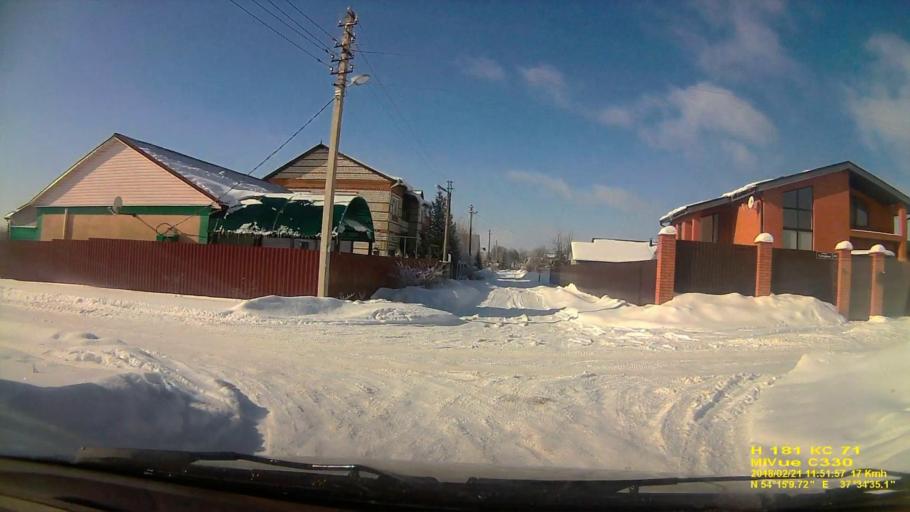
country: RU
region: Tula
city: Gorelki
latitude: 54.2530
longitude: 37.5764
